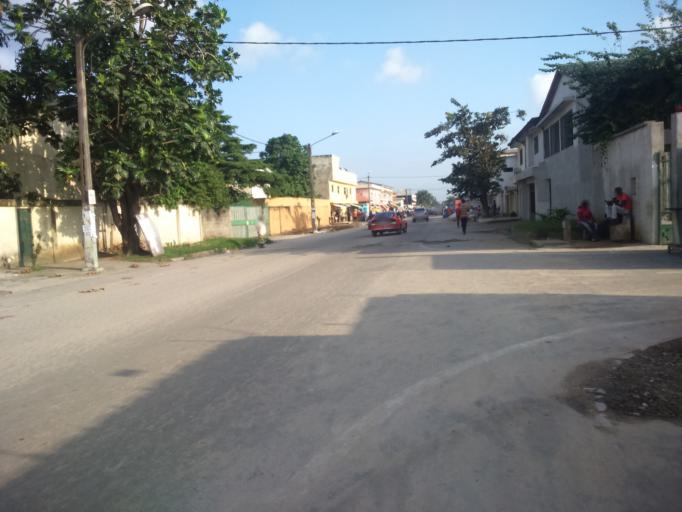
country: CI
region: Lagunes
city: Abobo
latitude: 5.4024
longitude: -3.9828
